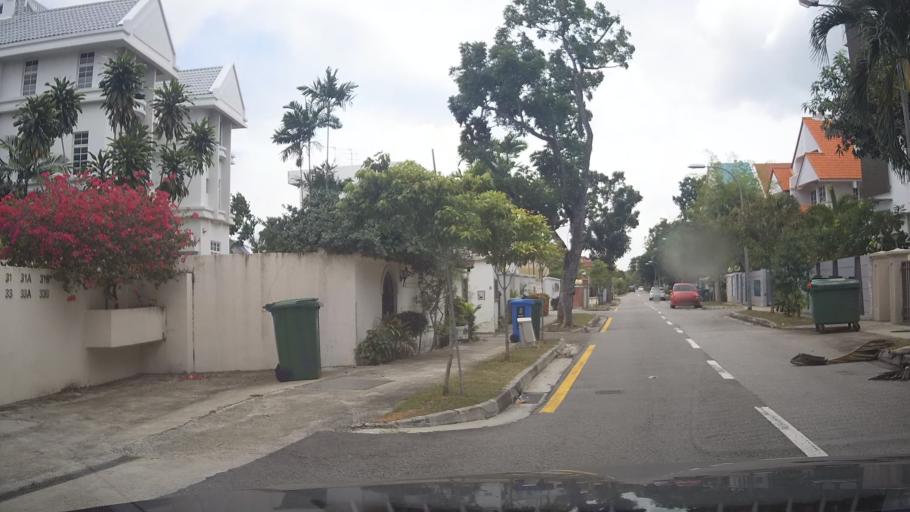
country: SG
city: Singapore
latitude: 1.3106
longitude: 103.9103
